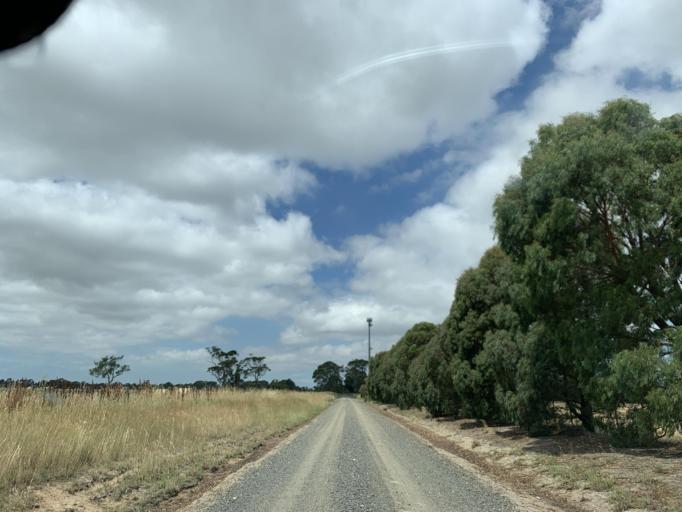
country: AU
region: Victoria
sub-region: Latrobe
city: Traralgon
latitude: -38.1156
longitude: 146.5702
